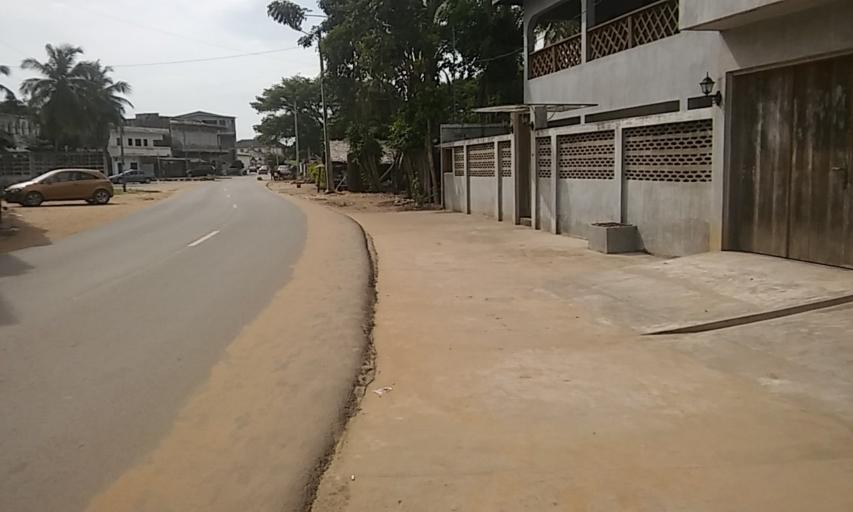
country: CI
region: Sud-Comoe
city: Grand-Bassam
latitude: 5.1962
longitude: -3.7297
